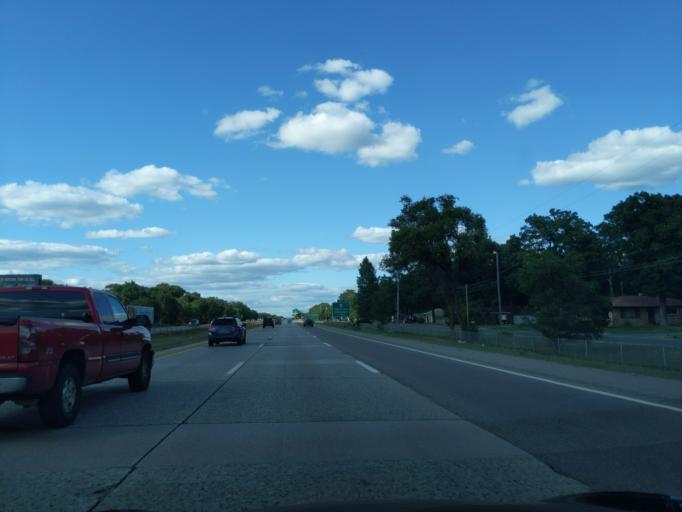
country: US
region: Michigan
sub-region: Muskegon County
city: Muskegon Heights
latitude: 43.2237
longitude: -86.2048
